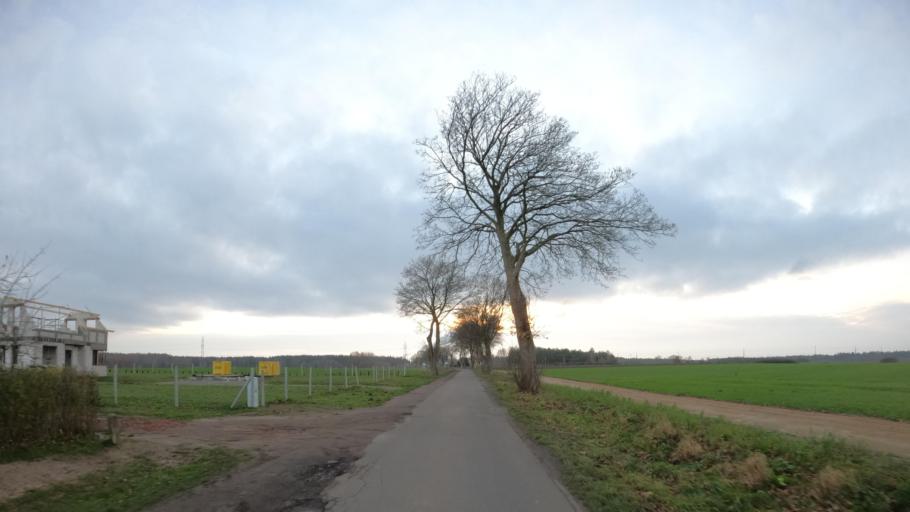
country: PL
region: West Pomeranian Voivodeship
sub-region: Powiat bialogardzki
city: Karlino
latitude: 54.0734
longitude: 15.8803
